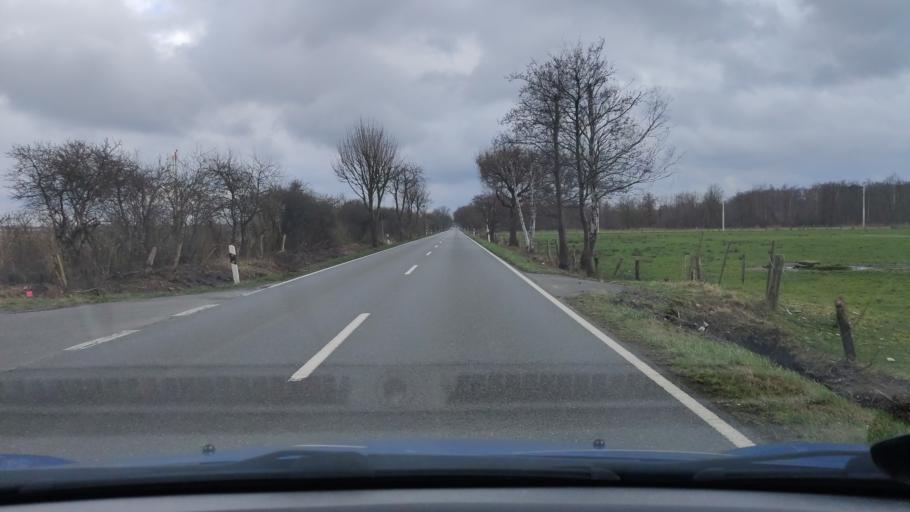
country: DE
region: Lower Saxony
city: Garbsen-Mitte
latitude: 52.4702
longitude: 9.6418
